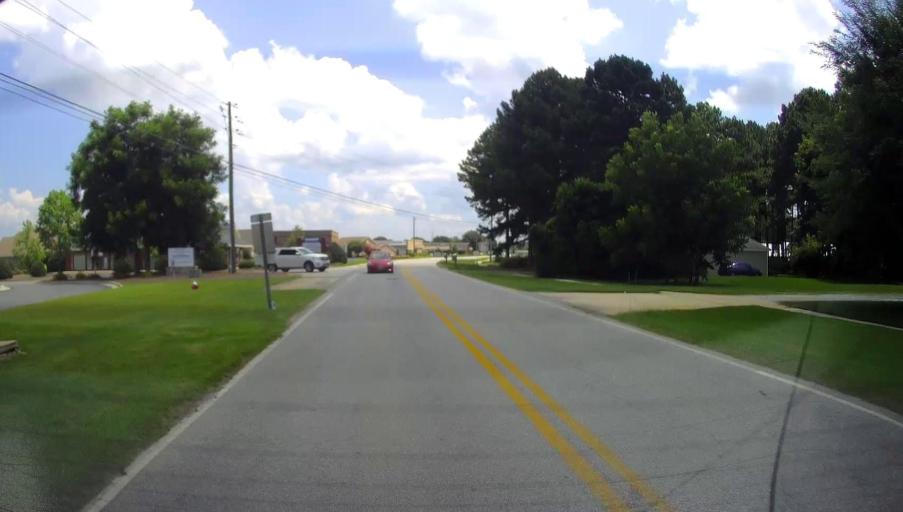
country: US
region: Georgia
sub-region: Houston County
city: Centerville
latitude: 32.6097
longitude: -83.6866
